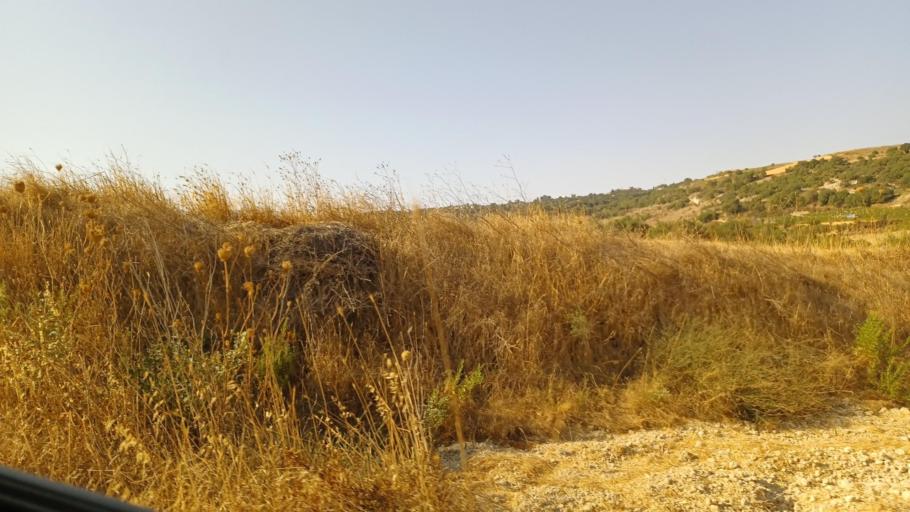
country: CY
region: Pafos
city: Tala
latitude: 34.9074
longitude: 32.4858
